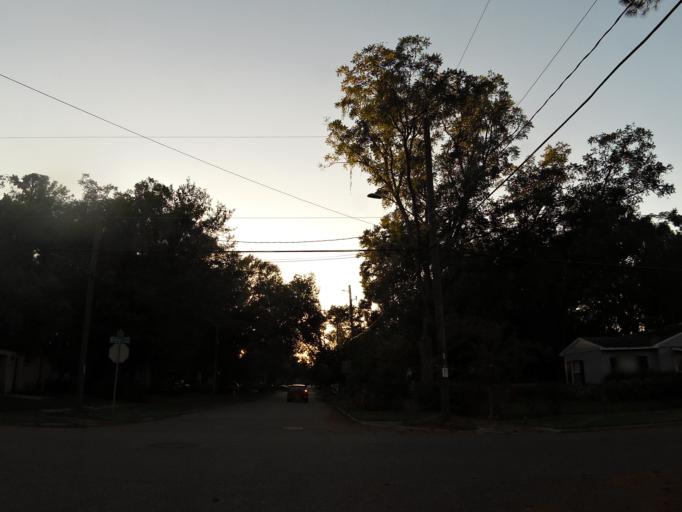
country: US
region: Florida
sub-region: Duval County
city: Jacksonville
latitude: 30.3146
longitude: -81.7094
